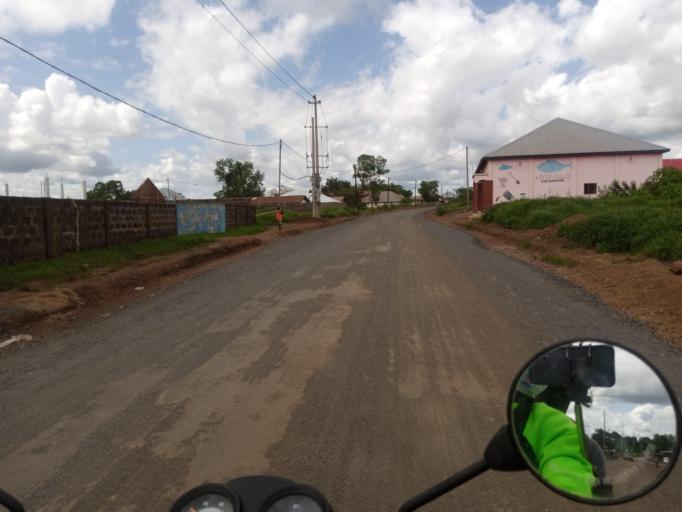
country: SL
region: Northern Province
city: Port Loko
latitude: 8.7734
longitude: -12.7744
